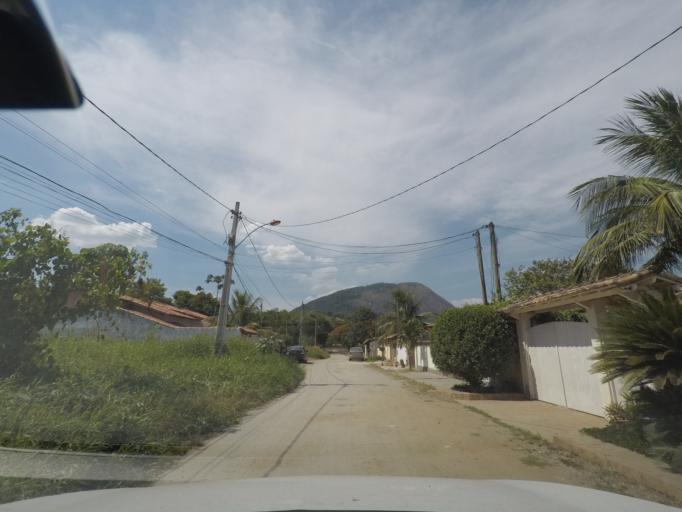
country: BR
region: Rio de Janeiro
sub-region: Marica
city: Marica
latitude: -22.9557
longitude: -42.9657
